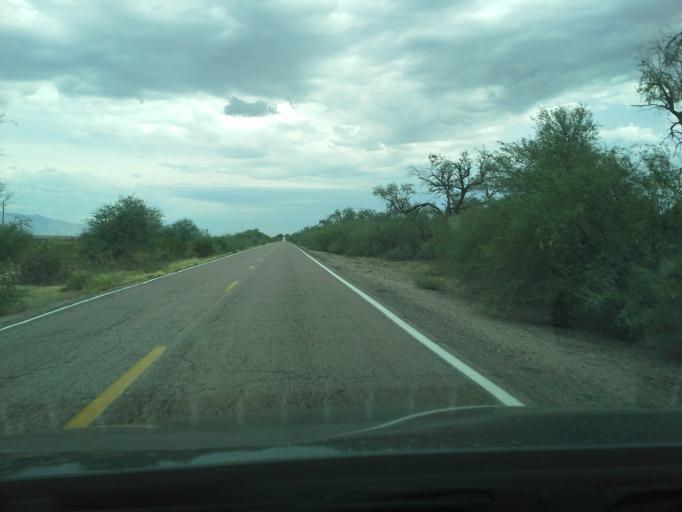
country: US
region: Arizona
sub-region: Pima County
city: Marana
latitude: 32.4745
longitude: -111.2328
